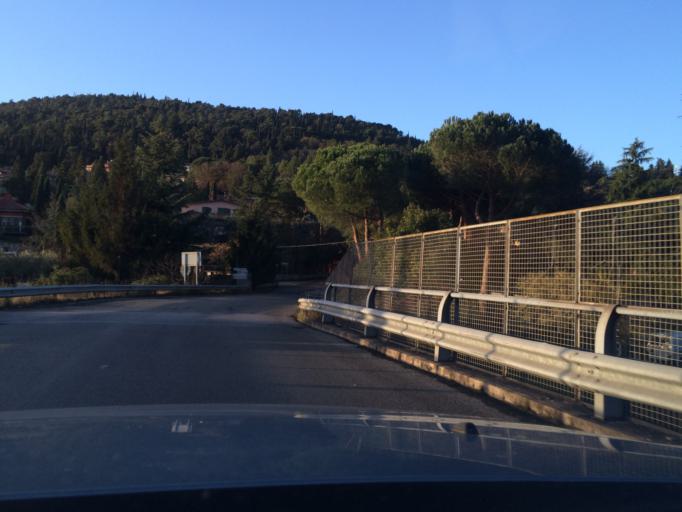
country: IT
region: Umbria
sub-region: Provincia di Perugia
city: Lacugnano
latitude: 43.1044
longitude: 12.3391
